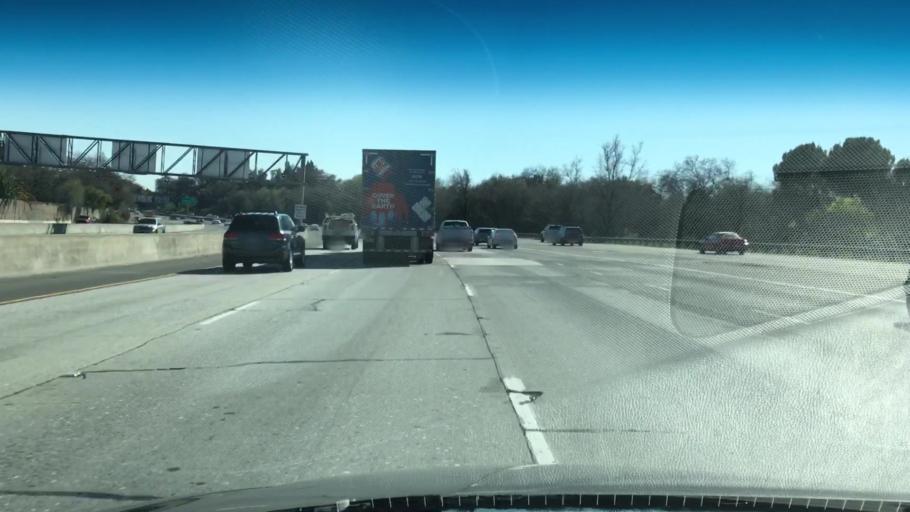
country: US
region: California
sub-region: Yolo County
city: West Sacramento
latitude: 38.5640
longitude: -121.5156
